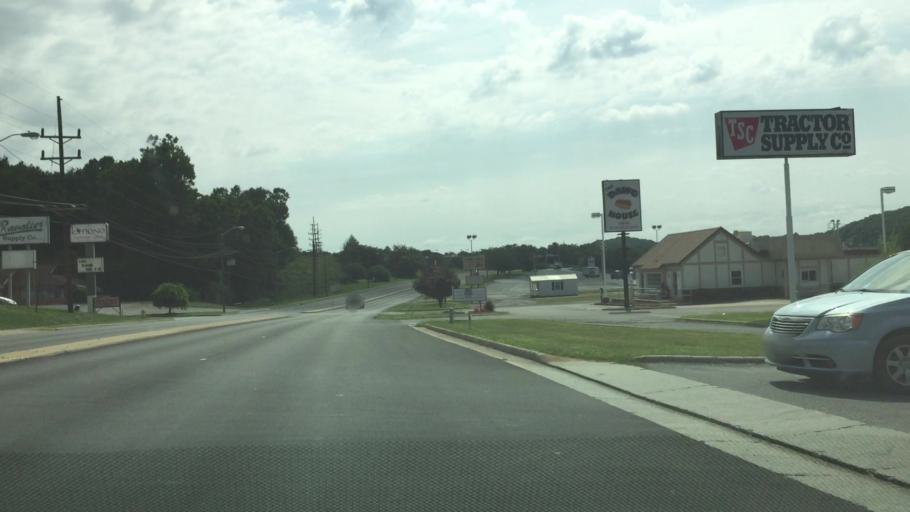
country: US
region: Virginia
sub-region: Pulaski County
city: Pulaski
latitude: 37.0483
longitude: -80.7593
